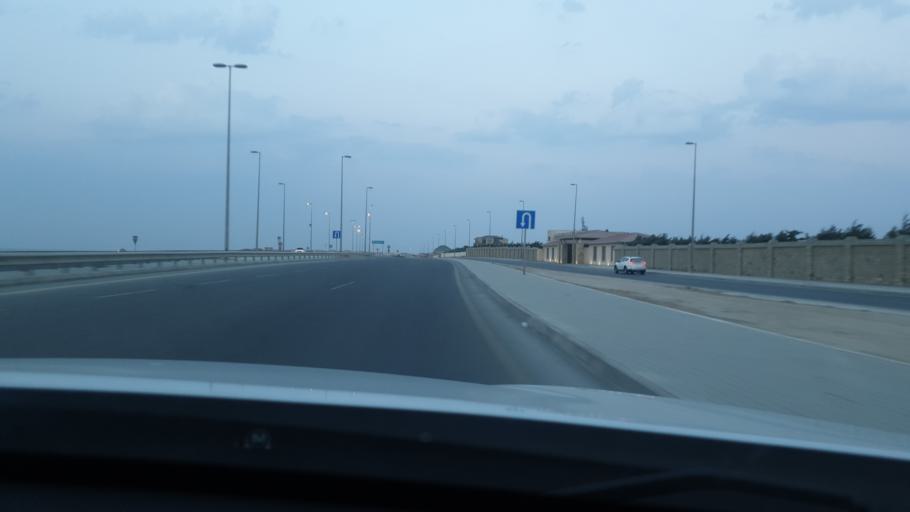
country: AZ
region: Baki
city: Bilajer
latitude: 40.5885
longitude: 50.0484
